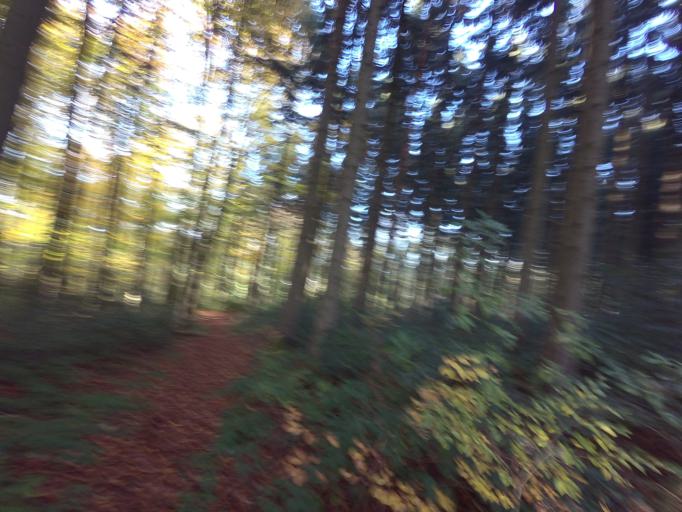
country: BE
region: Wallonia
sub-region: Province de Liege
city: Plombieres
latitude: 50.7742
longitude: 5.9607
